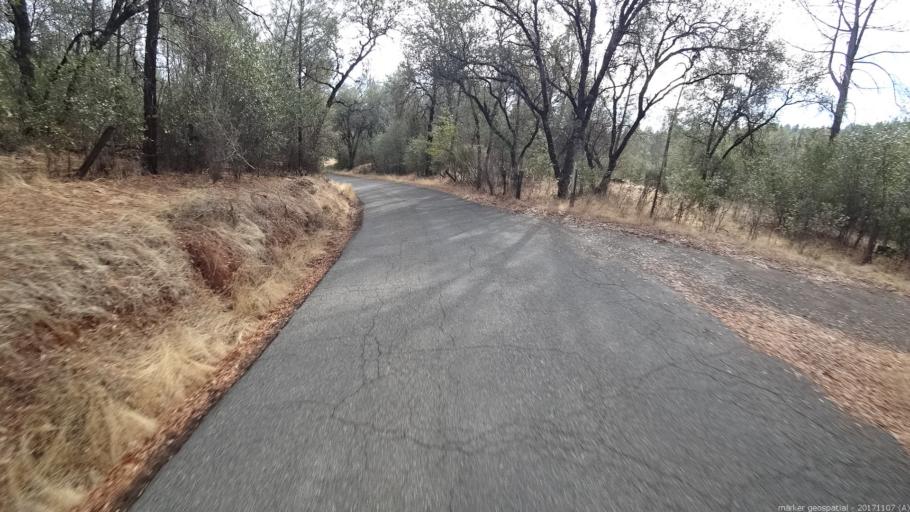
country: US
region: California
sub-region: Shasta County
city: Shasta
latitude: 40.5209
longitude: -122.5520
